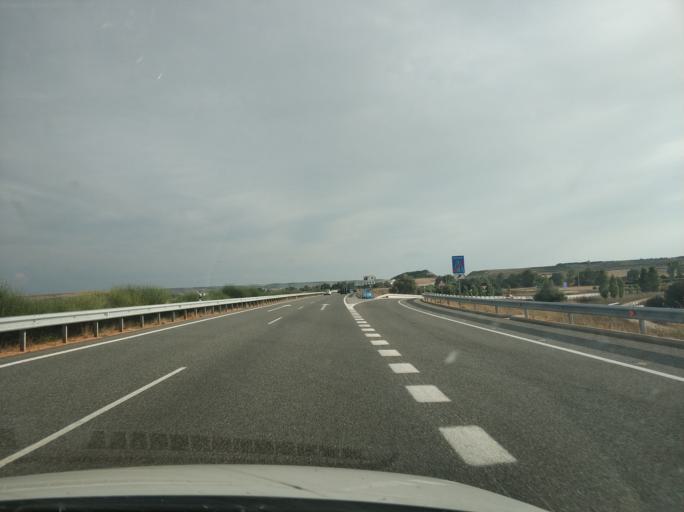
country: ES
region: Castille and Leon
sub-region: Provincia de Burgos
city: Quintanaortuno
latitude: 42.4663
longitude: -3.6883
